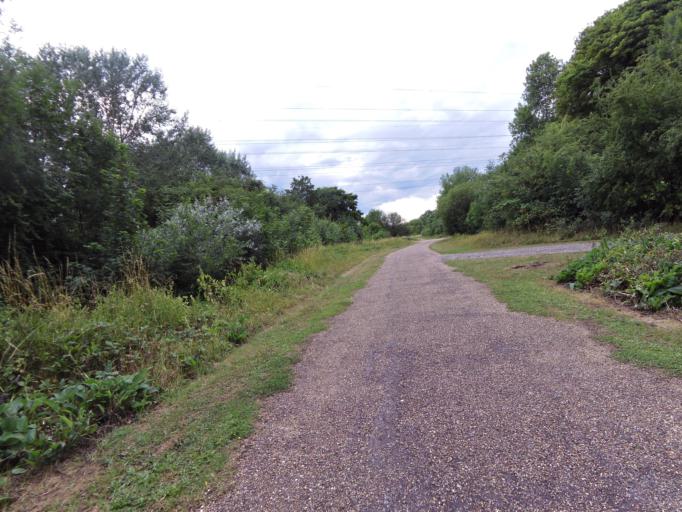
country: GB
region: England
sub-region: Essex
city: Waltham Abbey
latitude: 51.6939
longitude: -0.0129
